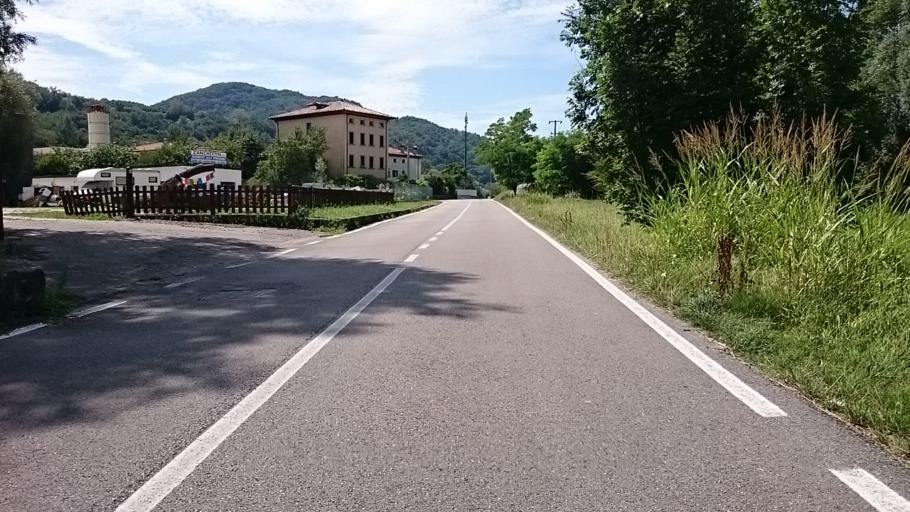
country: IT
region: Veneto
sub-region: Provincia di Treviso
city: Revine
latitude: 45.9951
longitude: 12.2505
